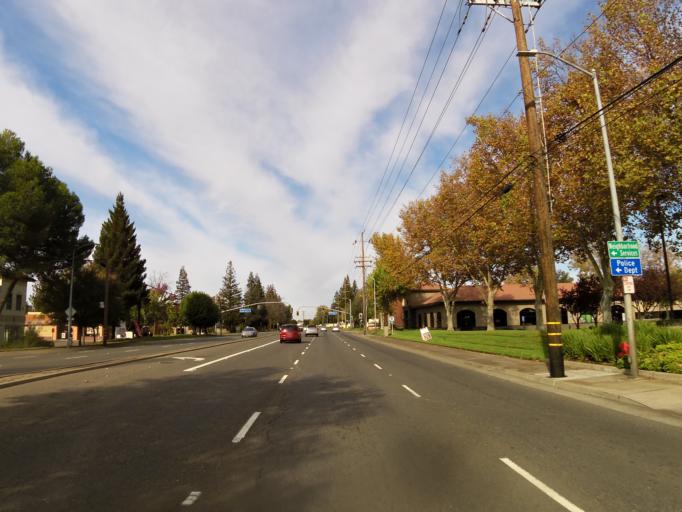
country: US
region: California
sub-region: Sacramento County
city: Gold River
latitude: 38.5968
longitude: -121.2656
